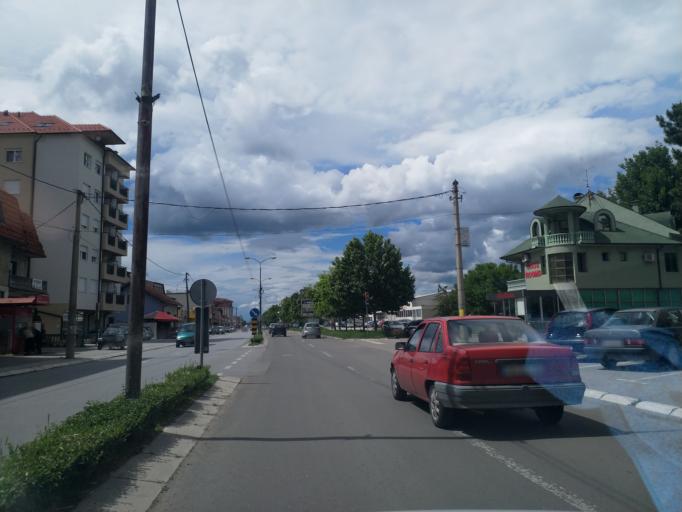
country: RS
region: Central Serbia
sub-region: Pomoravski Okrug
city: Paracin
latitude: 43.8655
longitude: 21.4077
